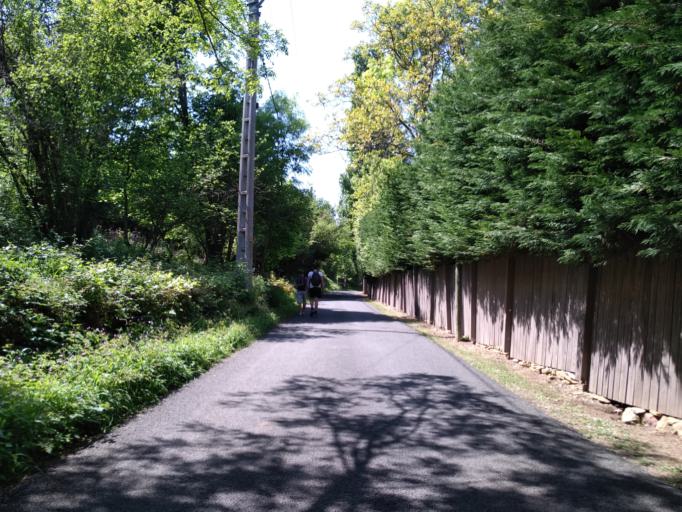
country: FR
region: Rhone-Alpes
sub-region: Departement du Rhone
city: Limonest
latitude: 45.8365
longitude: 4.8091
